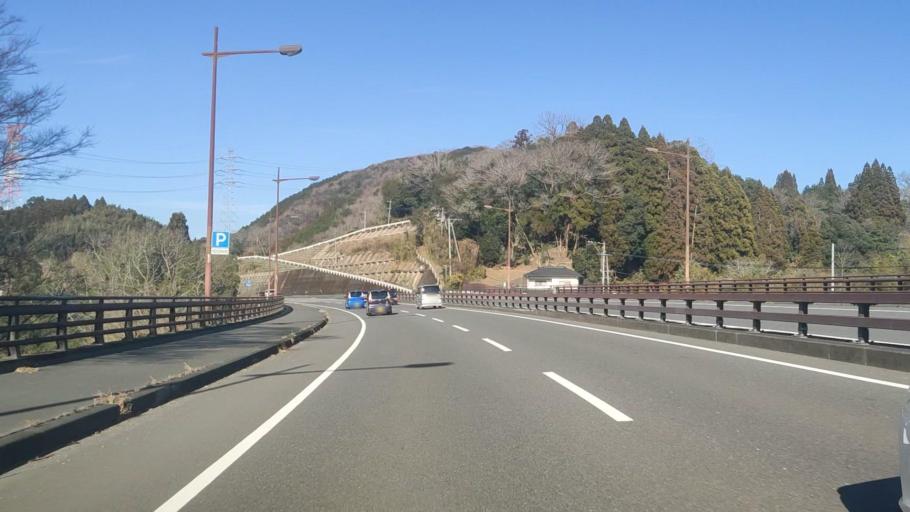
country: JP
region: Oita
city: Oita
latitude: 33.1094
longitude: 131.6566
